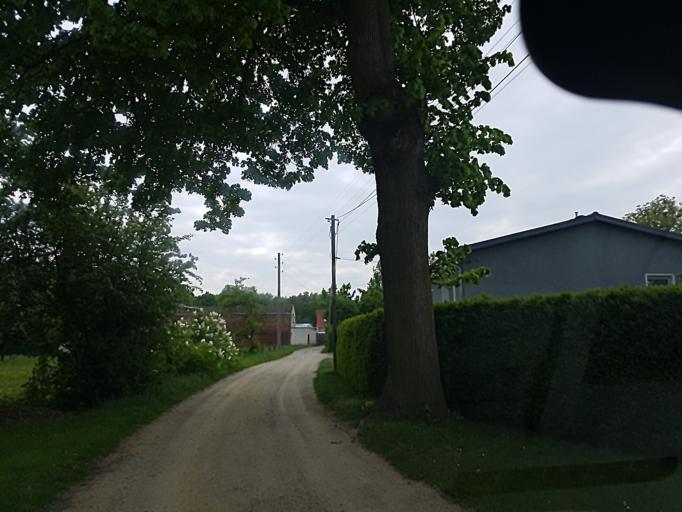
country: DE
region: Brandenburg
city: Finsterwalde
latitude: 51.5849
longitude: 13.7039
